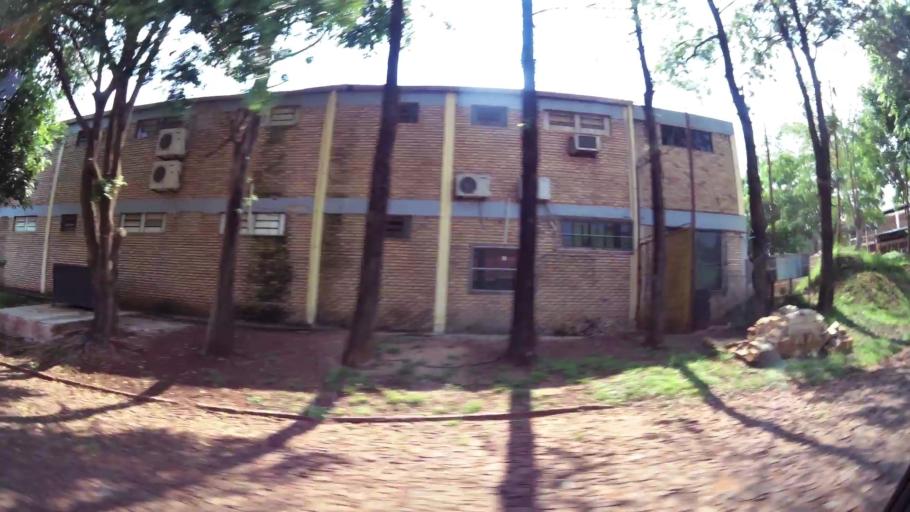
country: PY
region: Alto Parana
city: Ciudad del Este
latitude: -25.5152
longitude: -54.6235
